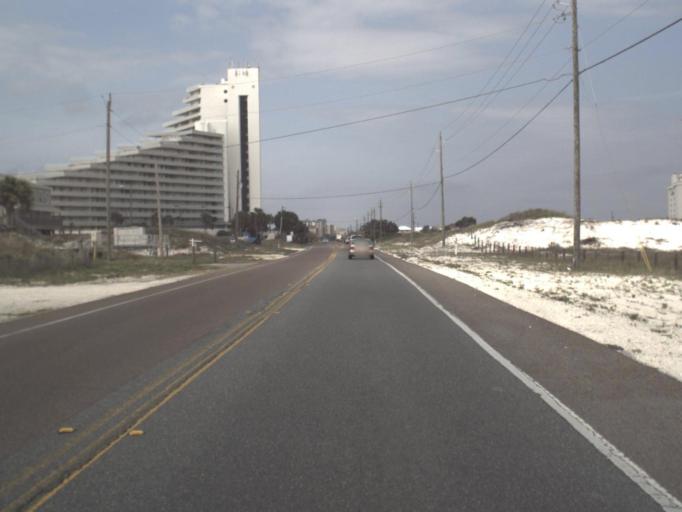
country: US
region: Alabama
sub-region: Baldwin County
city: Orange Beach
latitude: 30.2886
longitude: -87.4826
